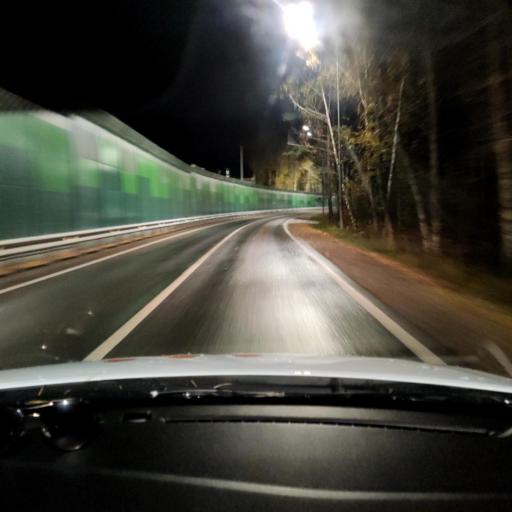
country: RU
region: Tatarstan
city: Verkhniy Uslon
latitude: 55.6280
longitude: 49.0141
